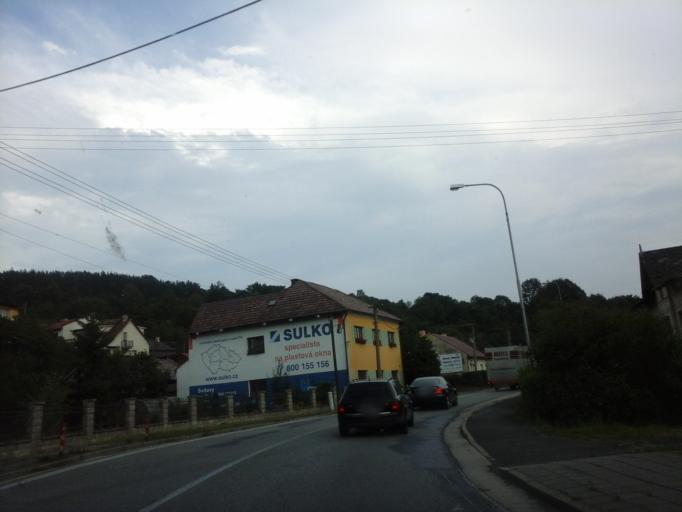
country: CZ
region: Pardubicky
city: Brnenec
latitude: 49.6193
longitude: 16.5305
